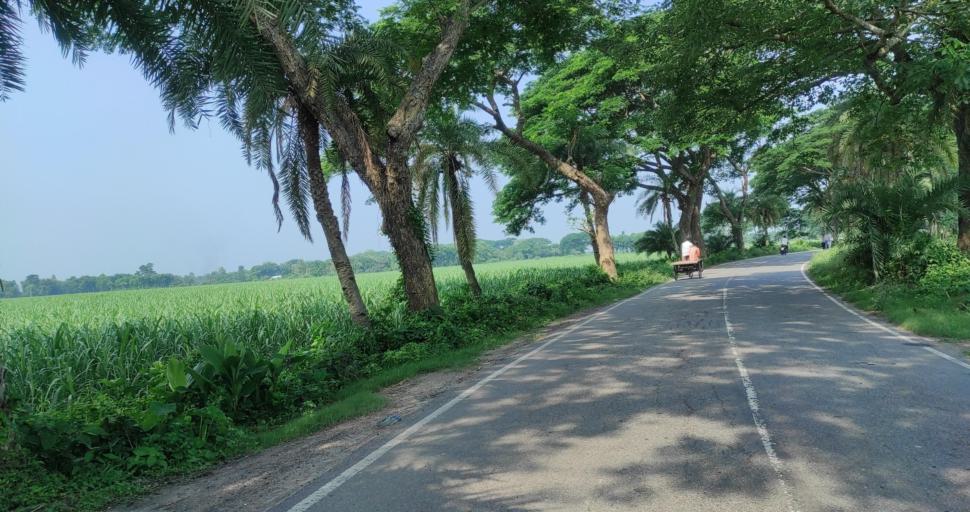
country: BD
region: Rajshahi
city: Ishurdi
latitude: 24.2786
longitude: 89.0623
